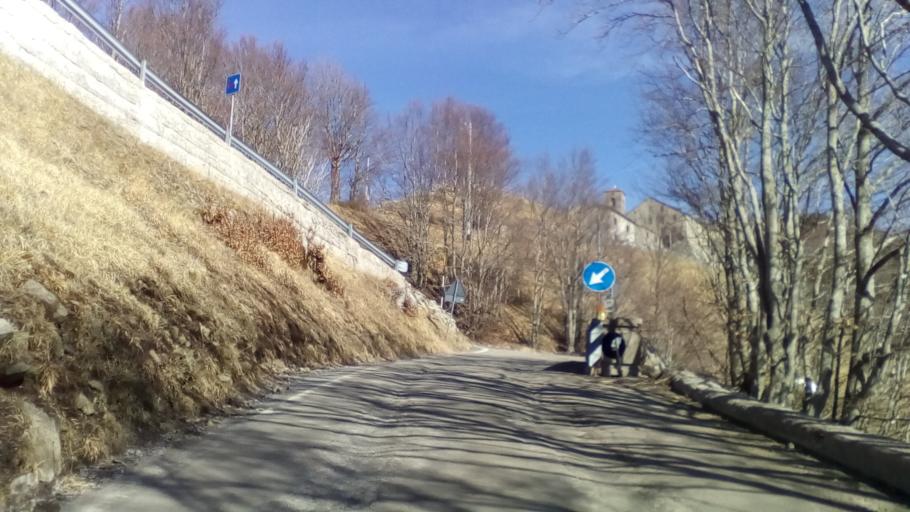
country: IT
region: Tuscany
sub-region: Provincia di Lucca
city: Fosciandora
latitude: 44.1876
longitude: 10.4794
